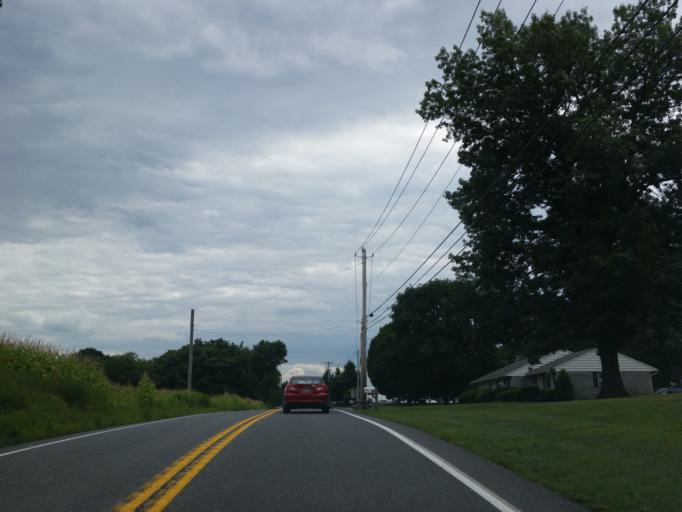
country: US
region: Pennsylvania
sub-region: Lancaster County
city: Swartzville
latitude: 40.2355
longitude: -76.0800
